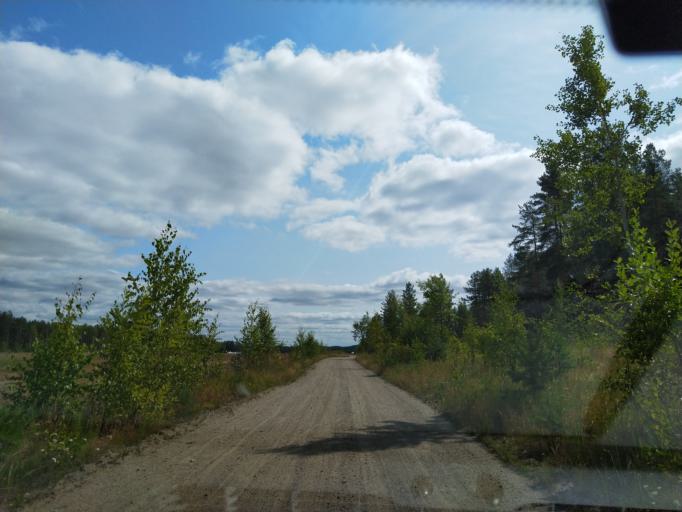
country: FI
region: Uusimaa
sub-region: Helsinki
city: Kaerkoelae
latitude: 60.7496
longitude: 24.0986
